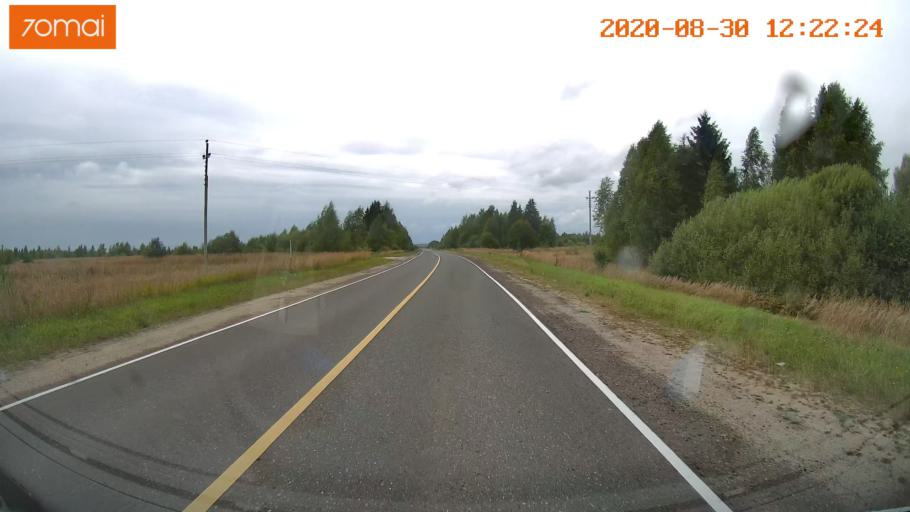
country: RU
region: Ivanovo
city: Yur'yevets
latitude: 57.3294
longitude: 42.8515
